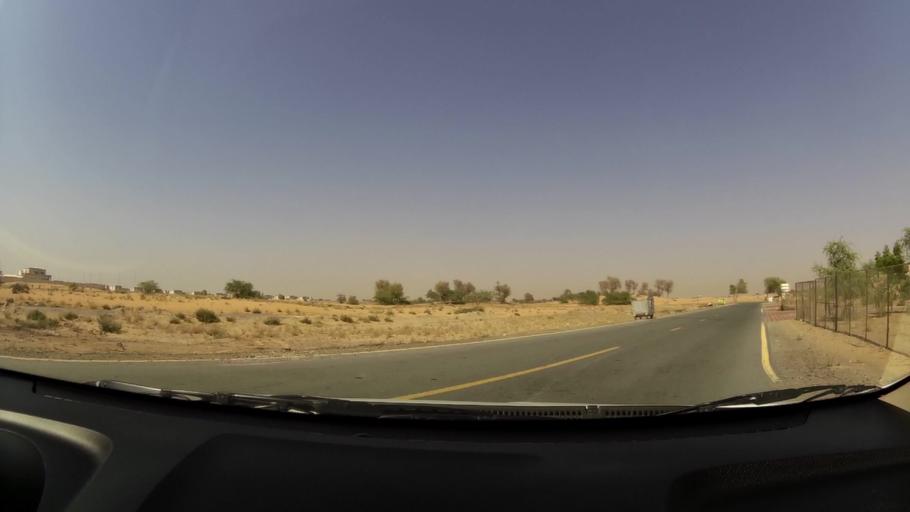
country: AE
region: Umm al Qaywayn
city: Umm al Qaywayn
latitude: 25.4780
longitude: 55.6149
